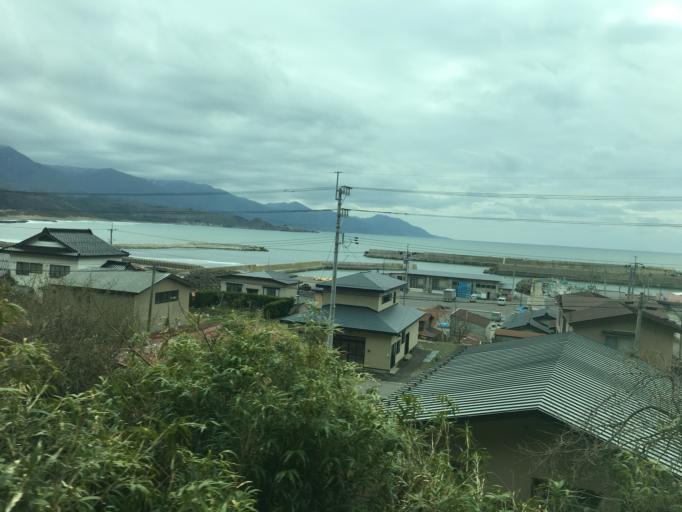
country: JP
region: Akita
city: Noshiromachi
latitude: 40.5879
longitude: 139.9134
